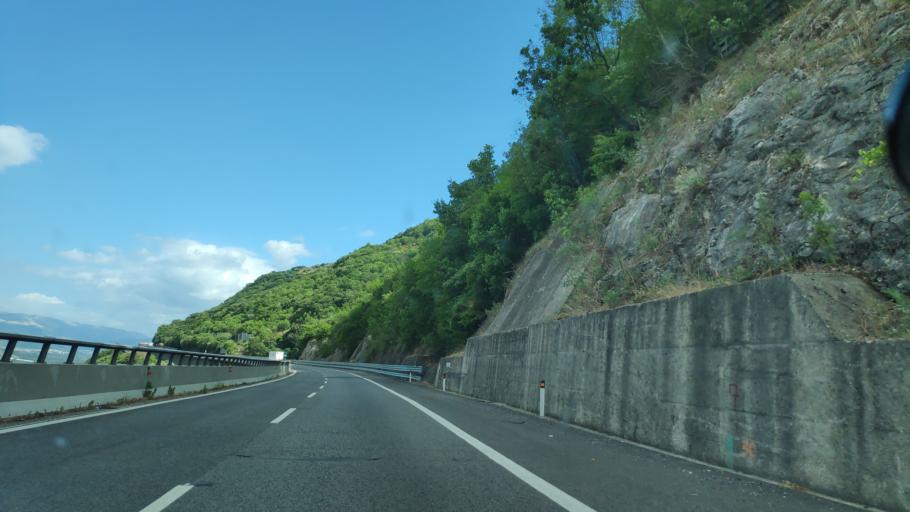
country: IT
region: Campania
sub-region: Provincia di Salerno
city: Sicignano degli Alburni
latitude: 40.5938
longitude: 15.3236
